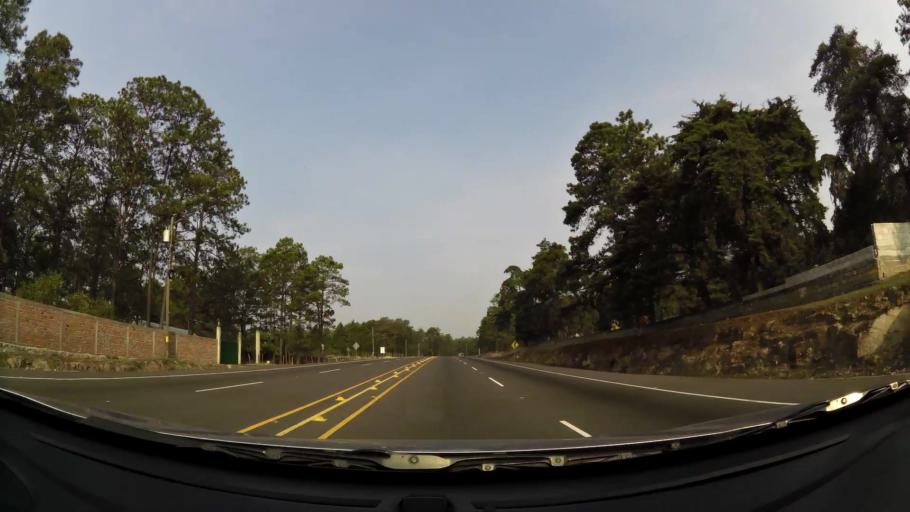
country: HN
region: Francisco Morazan
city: Zambrano
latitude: 14.2890
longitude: -87.4104
